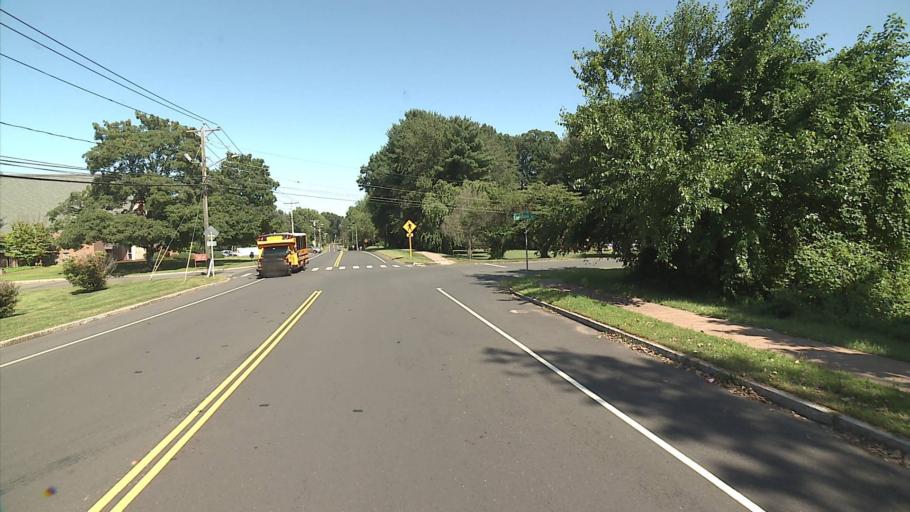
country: US
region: Connecticut
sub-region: Hartford County
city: Windsor
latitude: 41.8384
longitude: -72.6628
